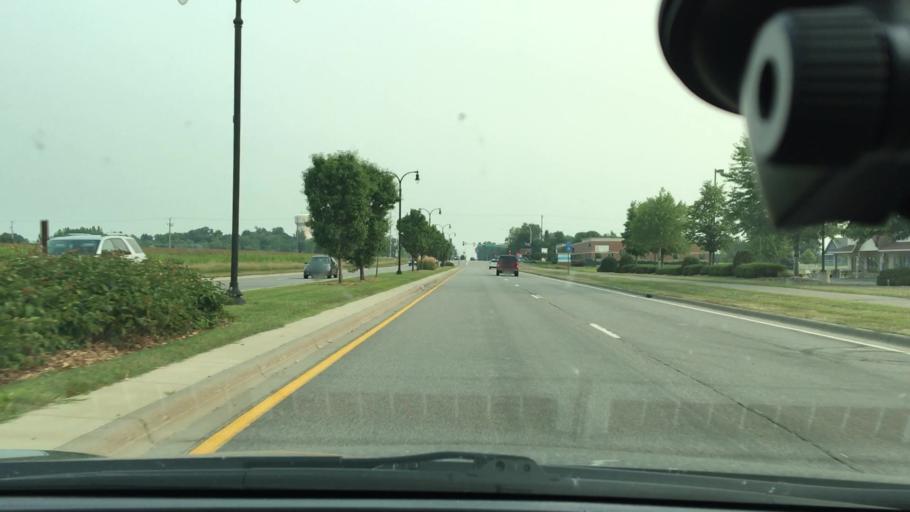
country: US
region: Minnesota
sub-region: Wright County
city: Albertville
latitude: 45.2274
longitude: -93.6645
